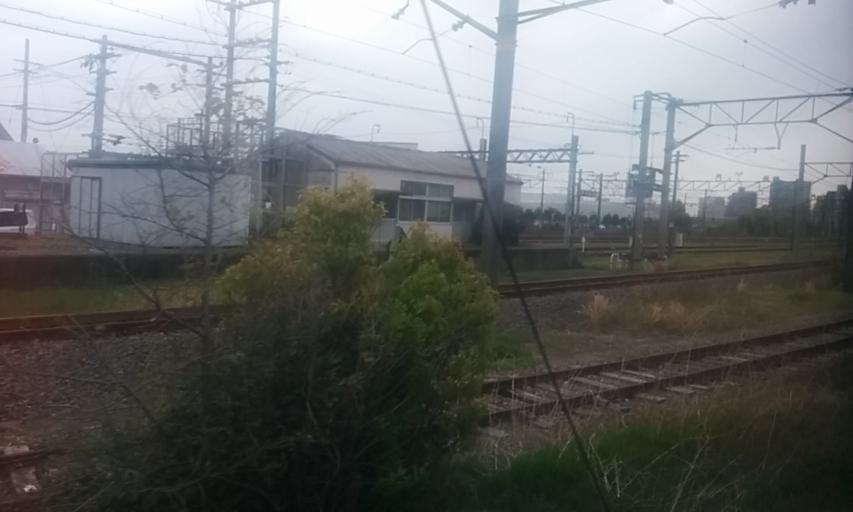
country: JP
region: Gifu
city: Ogaki
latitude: 35.3698
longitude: 136.6070
